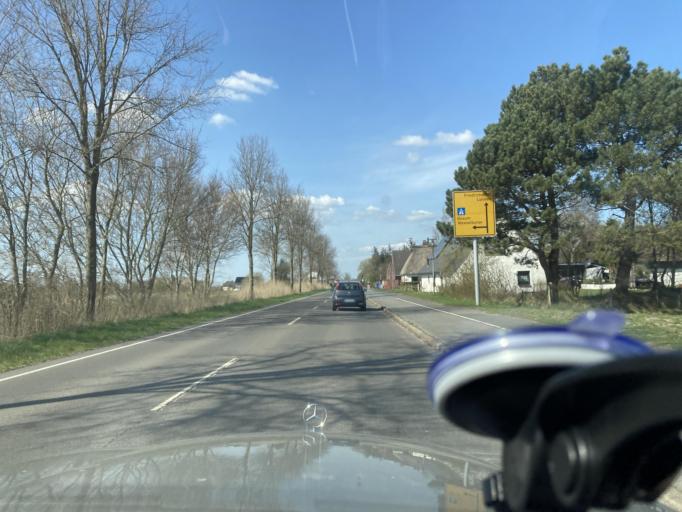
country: DE
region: Schleswig-Holstein
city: Krempel
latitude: 54.2960
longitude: 9.0399
